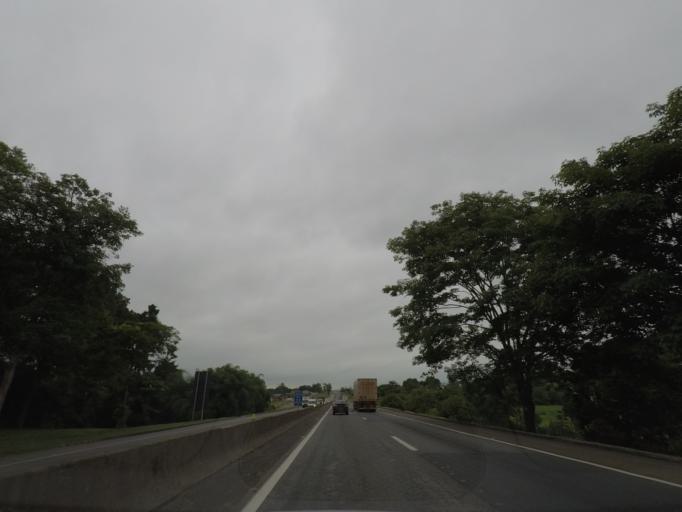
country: BR
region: Sao Paulo
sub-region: Pindamonhangaba
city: Pindamonhangaba
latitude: -22.9604
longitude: -45.4209
